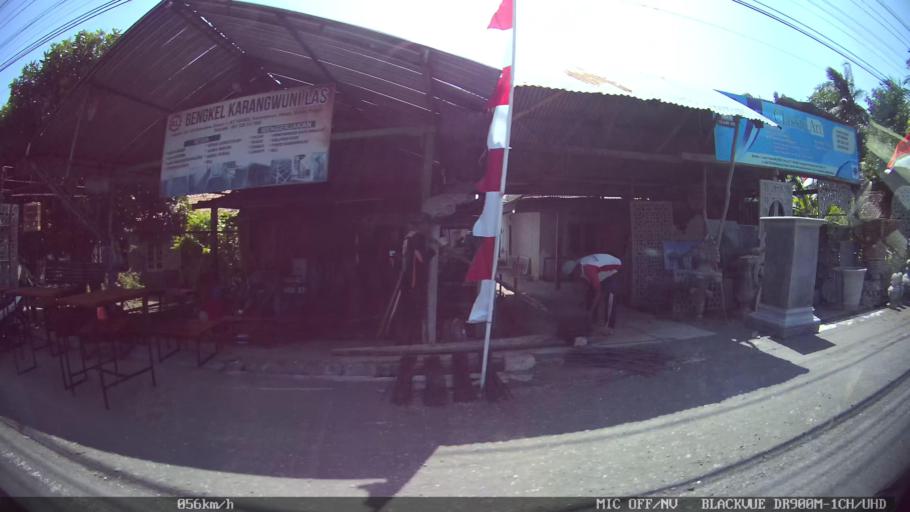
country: ID
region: Daerah Istimewa Yogyakarta
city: Srandakan
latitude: -7.9108
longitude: 110.0885
